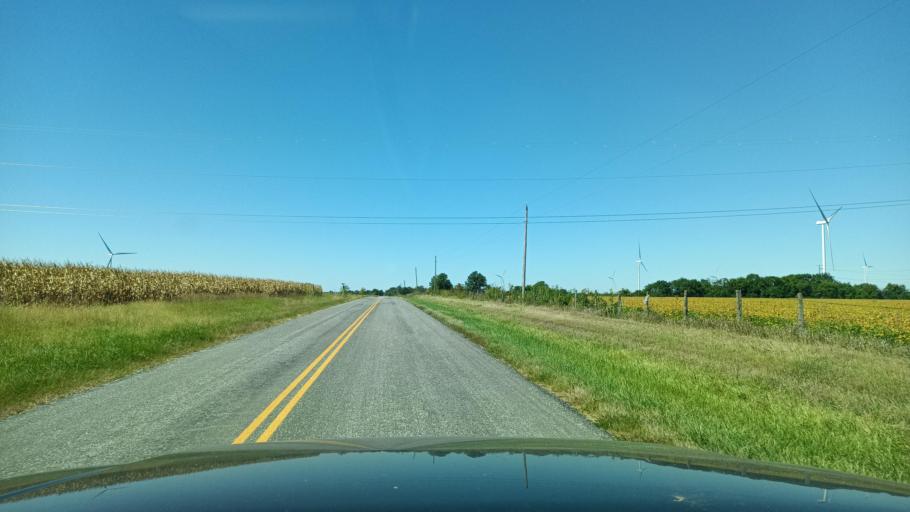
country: US
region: Missouri
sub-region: Adair County
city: Kirksville
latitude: 40.3306
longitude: -92.4914
